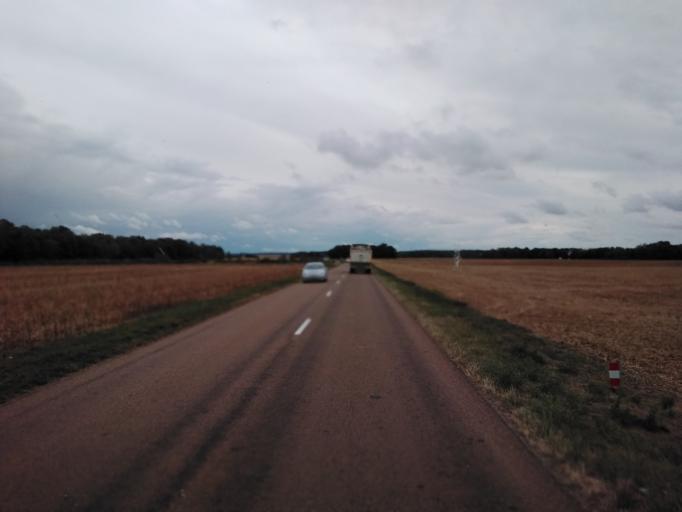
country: FR
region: Champagne-Ardenne
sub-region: Departement de l'Aube
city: Brienne-le-Chateau
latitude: 48.3427
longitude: 4.5296
